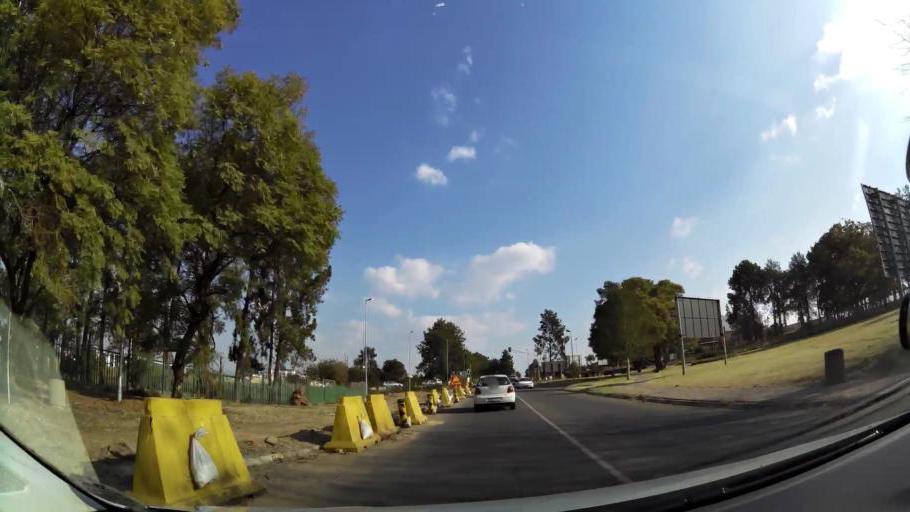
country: ZA
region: Gauteng
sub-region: City of Johannesburg Metropolitan Municipality
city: Modderfontein
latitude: -26.1074
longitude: 28.1483
